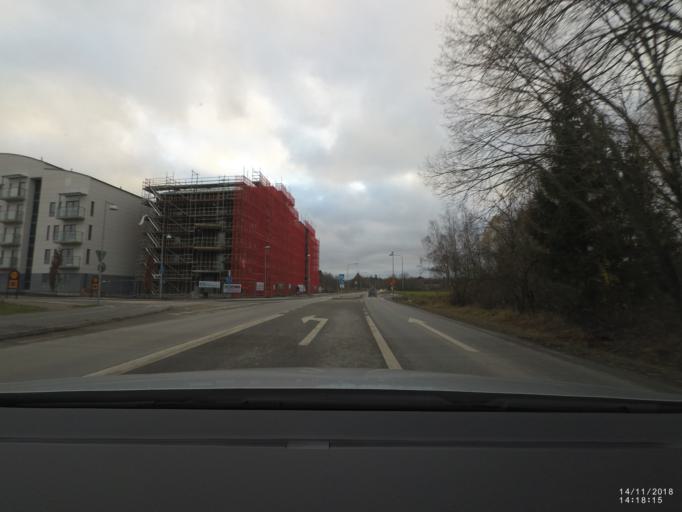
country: SE
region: Soedermanland
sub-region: Nykopings Kommun
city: Nykoping
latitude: 58.7401
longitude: 17.0061
